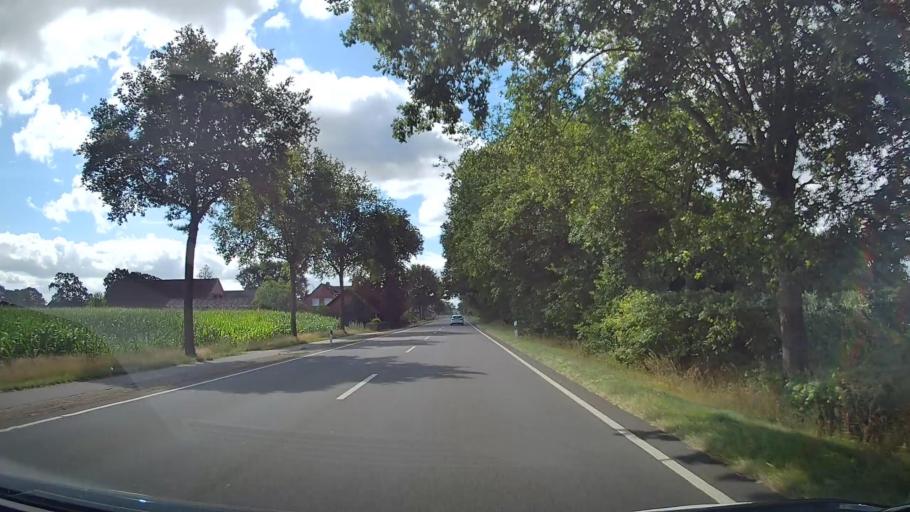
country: DE
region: Lower Saxony
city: Vechta
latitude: 52.6758
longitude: 8.3237
